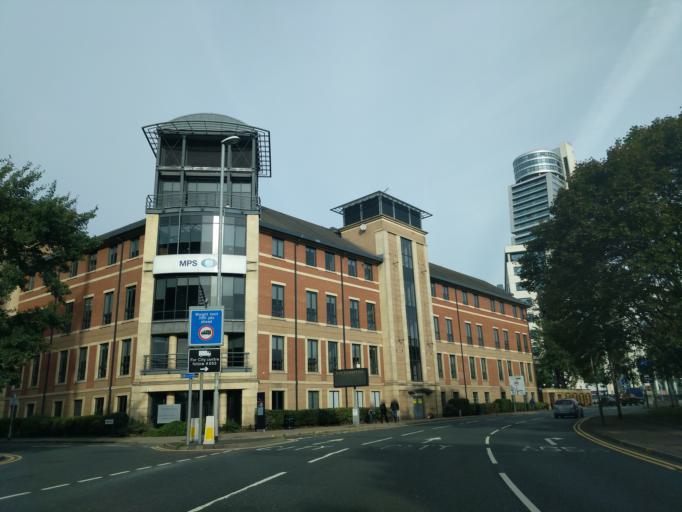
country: GB
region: England
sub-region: City and Borough of Leeds
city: Leeds
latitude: 53.7899
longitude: -1.5471
